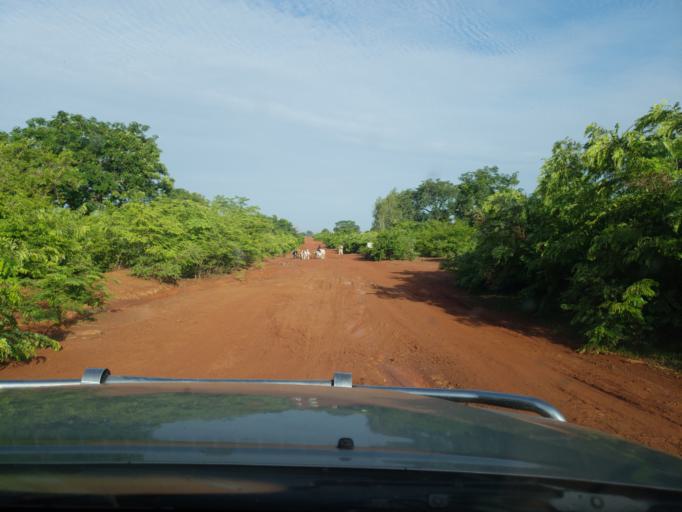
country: ML
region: Sikasso
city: Koutiala
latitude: 12.4242
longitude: -5.6645
